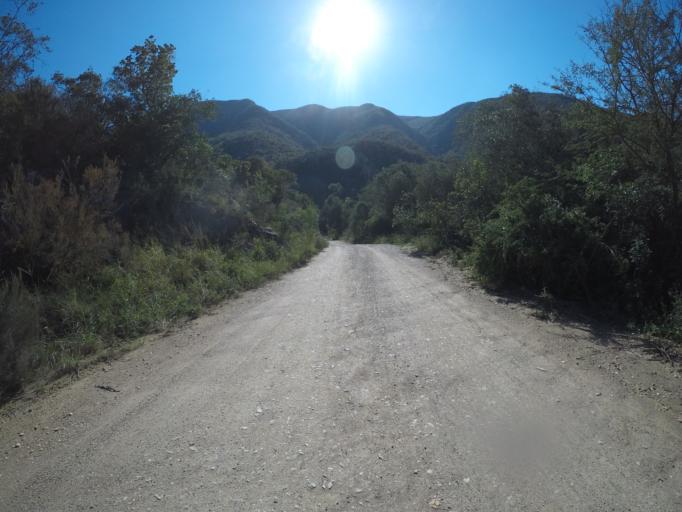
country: ZA
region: Eastern Cape
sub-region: Cacadu District Municipality
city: Kareedouw
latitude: -33.6578
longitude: 24.5260
